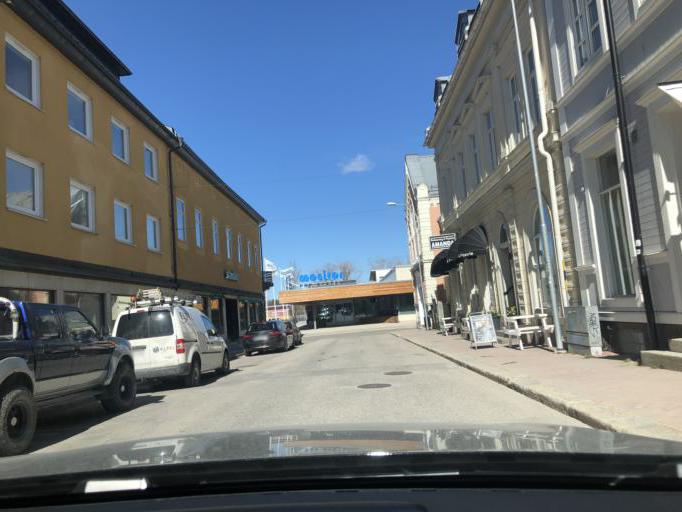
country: SE
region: Gaevleborg
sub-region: Hudiksvalls Kommun
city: Hudiksvall
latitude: 61.7282
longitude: 17.1086
